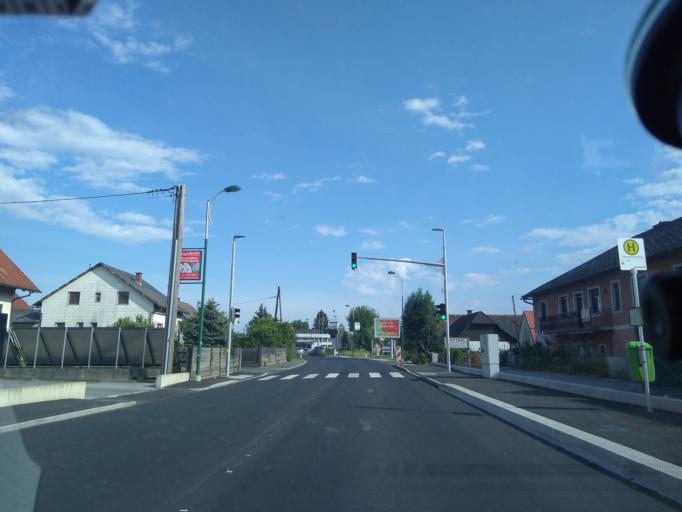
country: AT
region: Styria
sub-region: Politischer Bezirk Graz-Umgebung
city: Feldkirchen bei Graz
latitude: 47.0142
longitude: 15.4744
